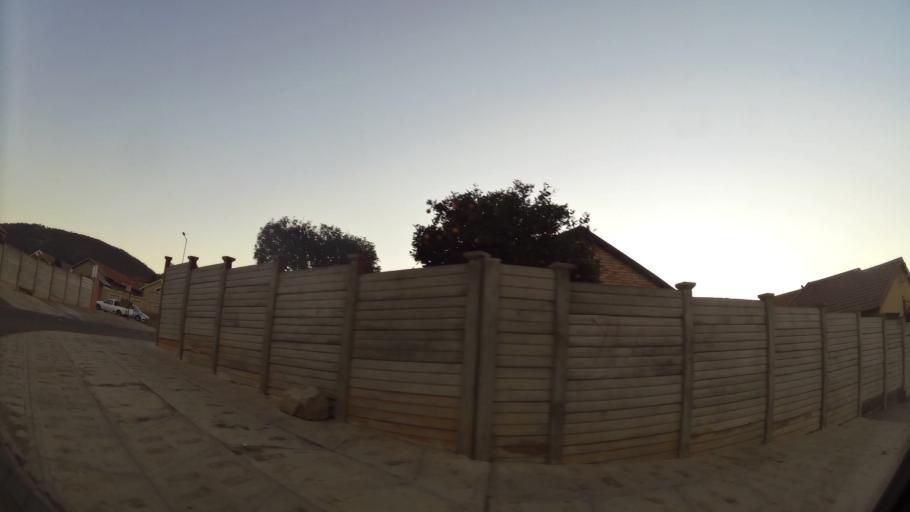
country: ZA
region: North-West
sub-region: Bojanala Platinum District Municipality
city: Rustenburg
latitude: -25.6529
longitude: 27.2024
